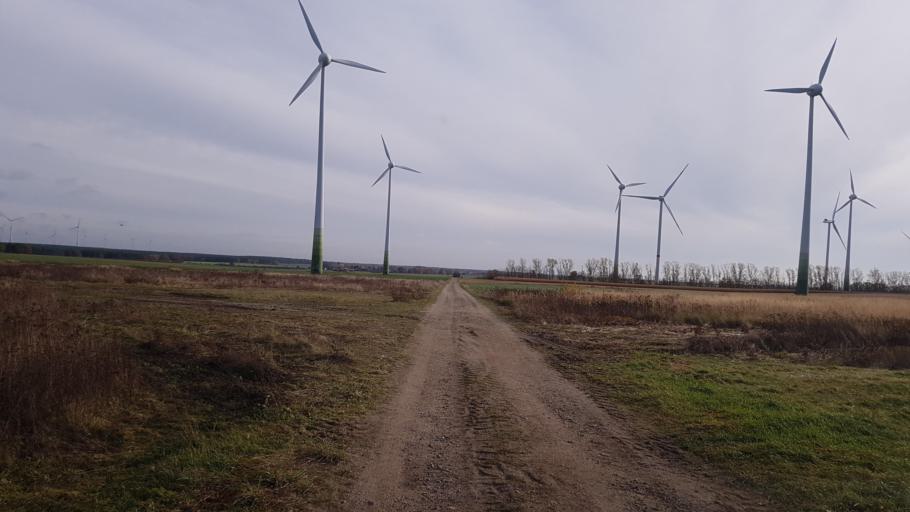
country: DE
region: Brandenburg
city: Treuenbrietzen
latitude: 52.0164
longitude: 12.8927
